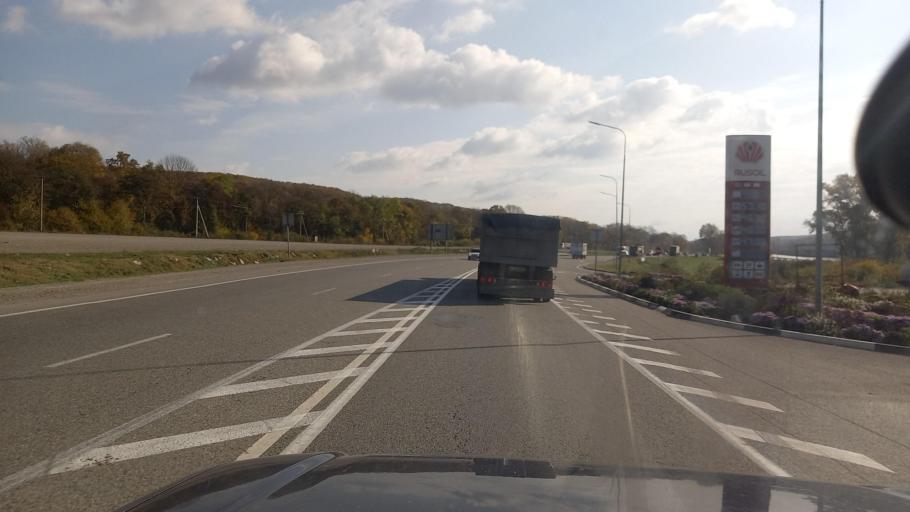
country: RU
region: Krasnodarskiy
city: Gayduk
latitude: 44.8767
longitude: 37.7817
